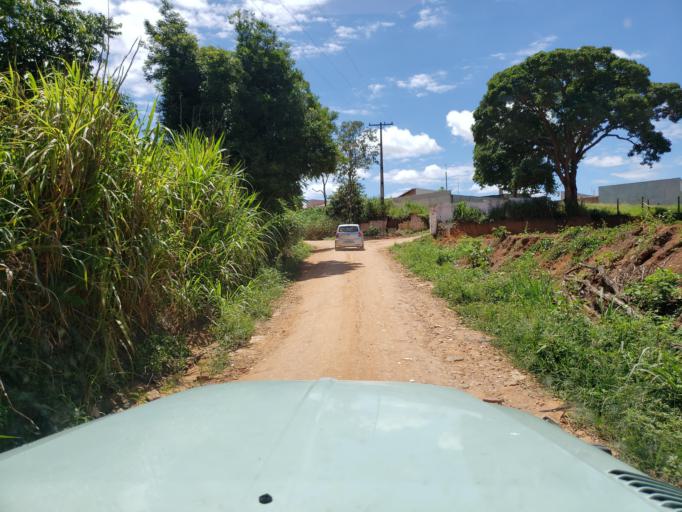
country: BR
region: Sao Paulo
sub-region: Moji-Guacu
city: Mogi-Gaucu
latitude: -22.3020
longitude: -46.9005
